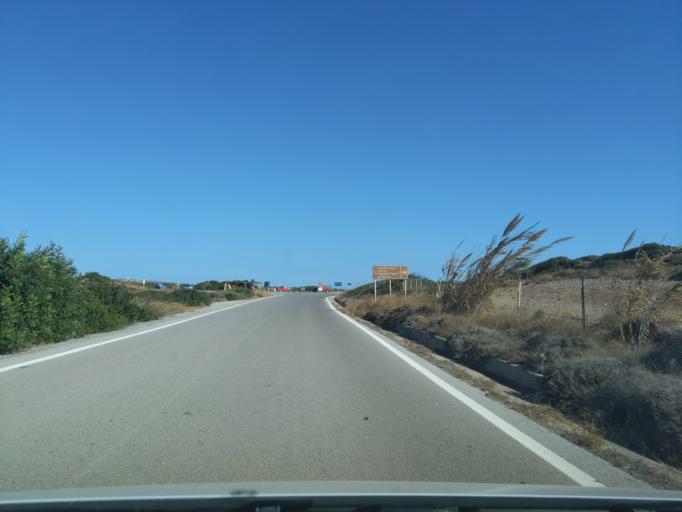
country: GR
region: Crete
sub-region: Nomos Lasithiou
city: Palekastro
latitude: 35.2403
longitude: 26.2481
